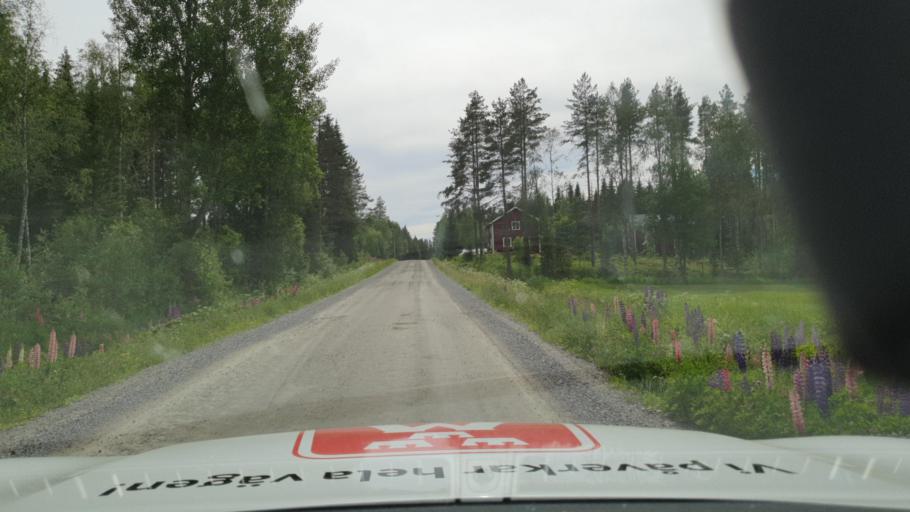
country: SE
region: Vaesterbotten
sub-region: Skelleftea Kommun
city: Burea
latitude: 64.4681
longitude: 21.0537
